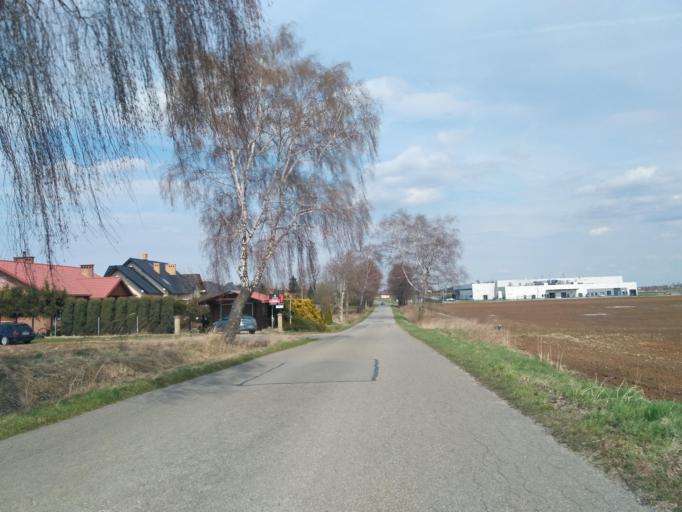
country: PL
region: Subcarpathian Voivodeship
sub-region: Powiat ropczycko-sedziszowski
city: Sedziszow Malopolski
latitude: 50.0574
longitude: 21.7145
